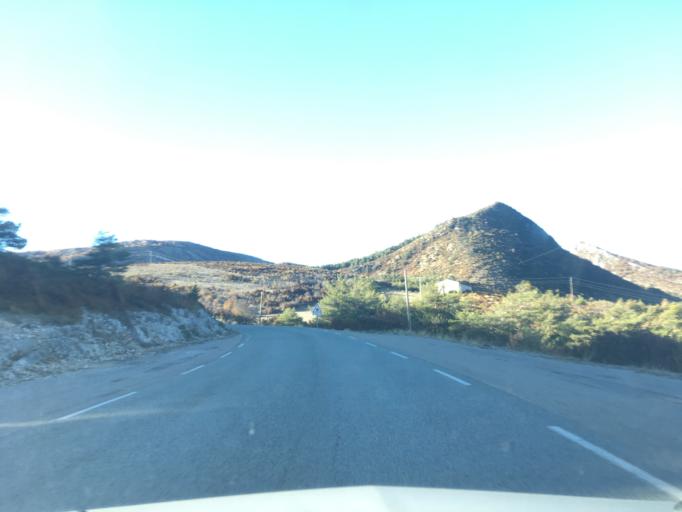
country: FR
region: Provence-Alpes-Cote d'Azur
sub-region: Departement des Alpes-de-Haute-Provence
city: Castellane
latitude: 43.7511
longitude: 6.4190
